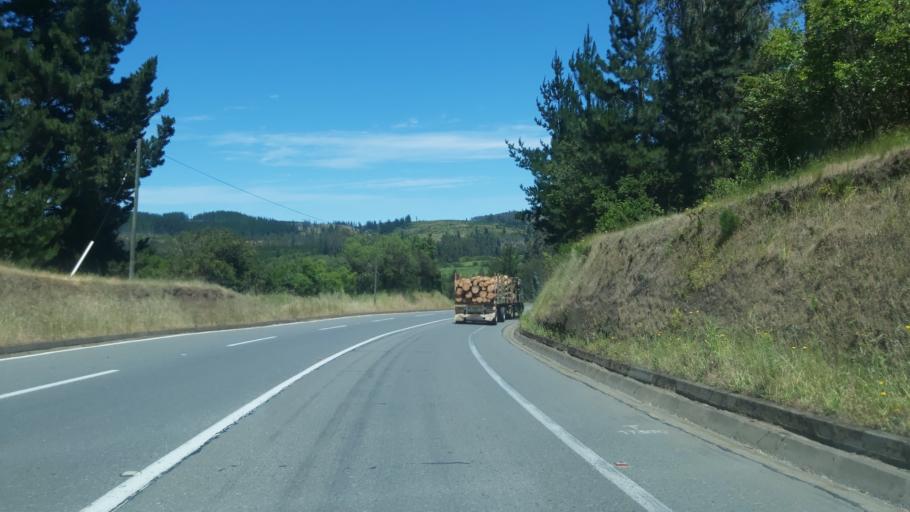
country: CL
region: Maule
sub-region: Provincia de Talca
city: Constitucion
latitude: -35.1538
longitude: -72.2222
